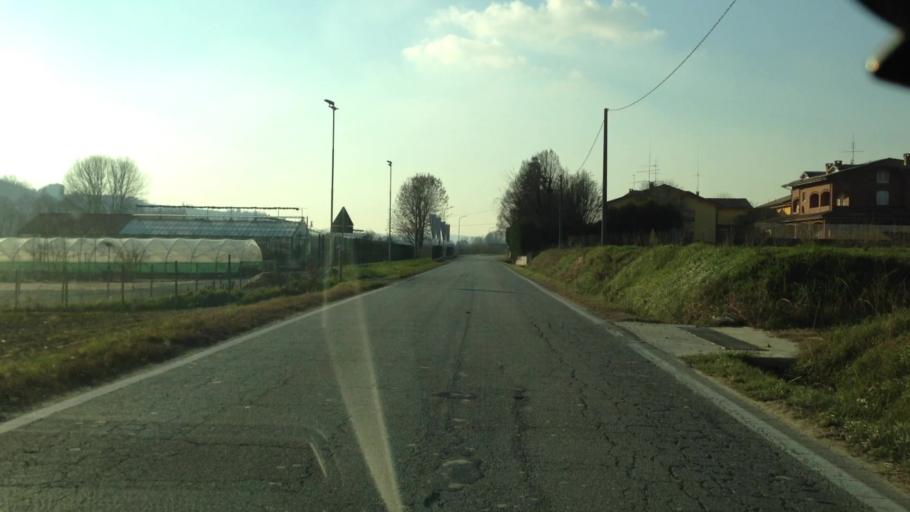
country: IT
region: Piedmont
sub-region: Provincia di Asti
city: Mombercelli
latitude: 44.8270
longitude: 8.3100
